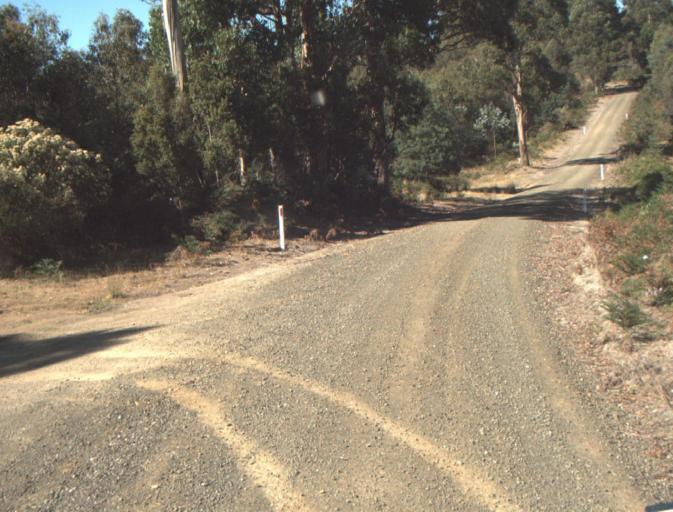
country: AU
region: Tasmania
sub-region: Dorset
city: Scottsdale
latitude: -41.2708
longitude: 147.3763
